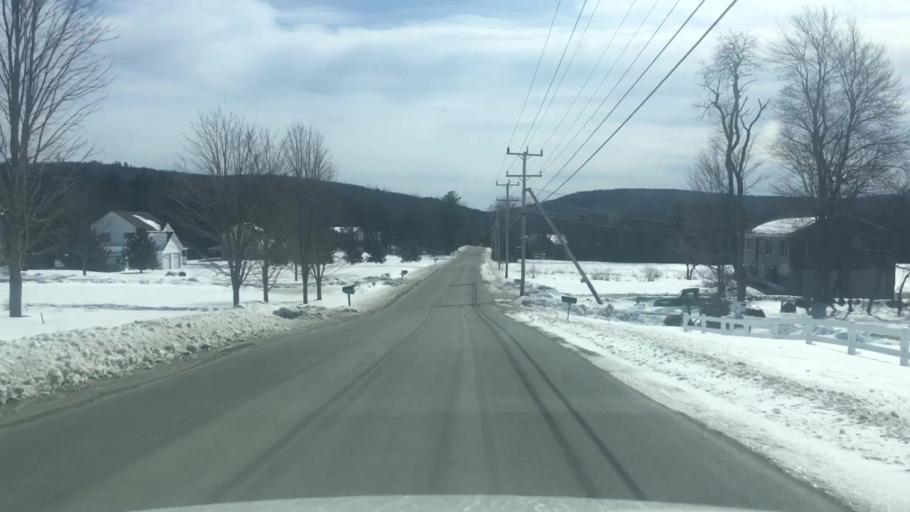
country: US
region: Maine
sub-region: Penobscot County
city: Holden
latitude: 44.7453
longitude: -68.6311
